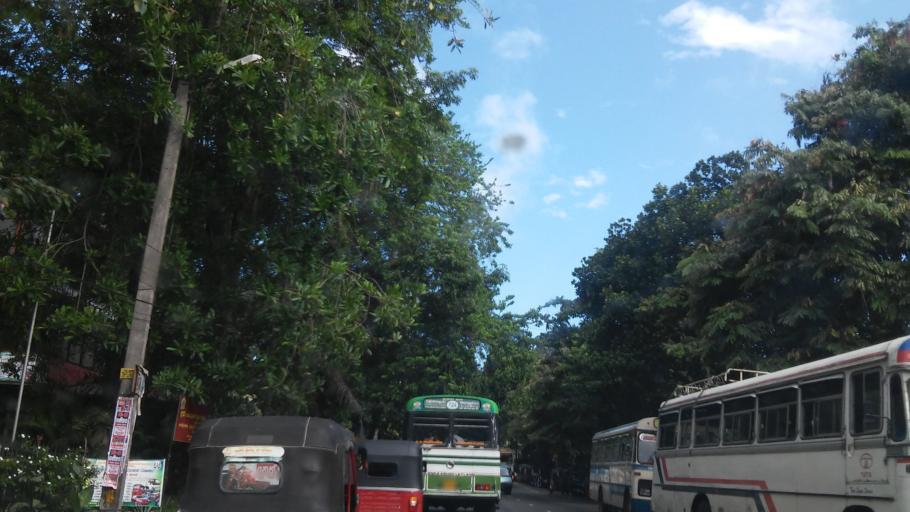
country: LK
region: Central
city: Kandy
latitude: 7.2679
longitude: 80.5991
